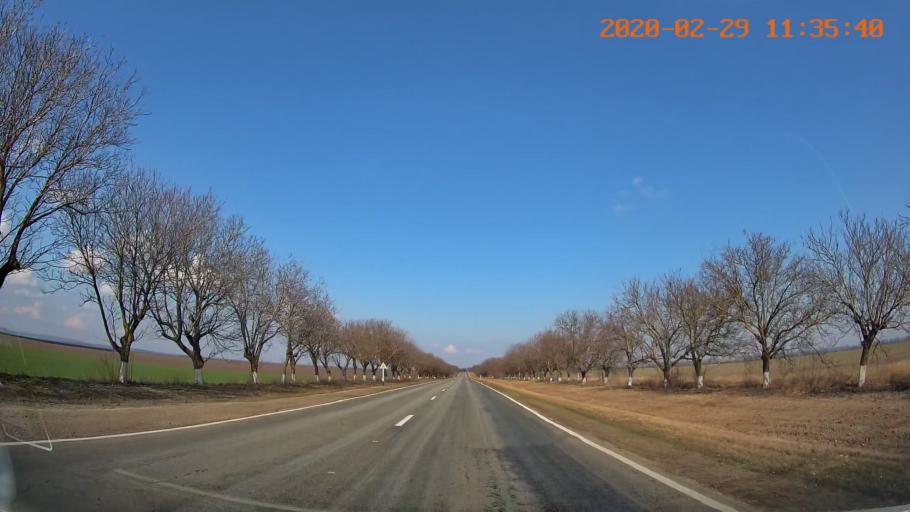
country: MD
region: Rezina
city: Saharna
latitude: 47.5840
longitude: 29.0618
